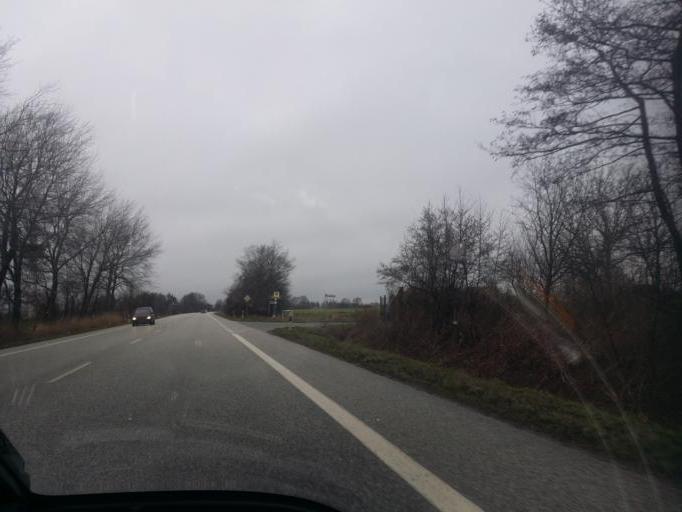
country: DE
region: Schleswig-Holstein
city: Bordelum
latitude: 54.6402
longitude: 8.9488
